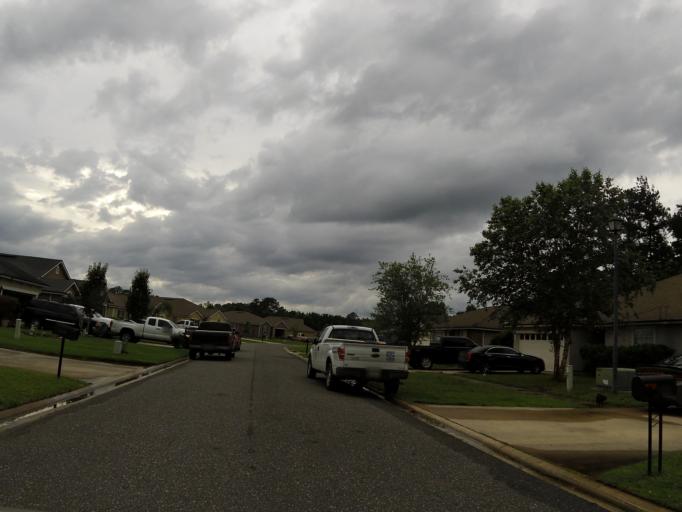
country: US
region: Florida
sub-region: Nassau County
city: Callahan
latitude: 30.5716
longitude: -81.8286
